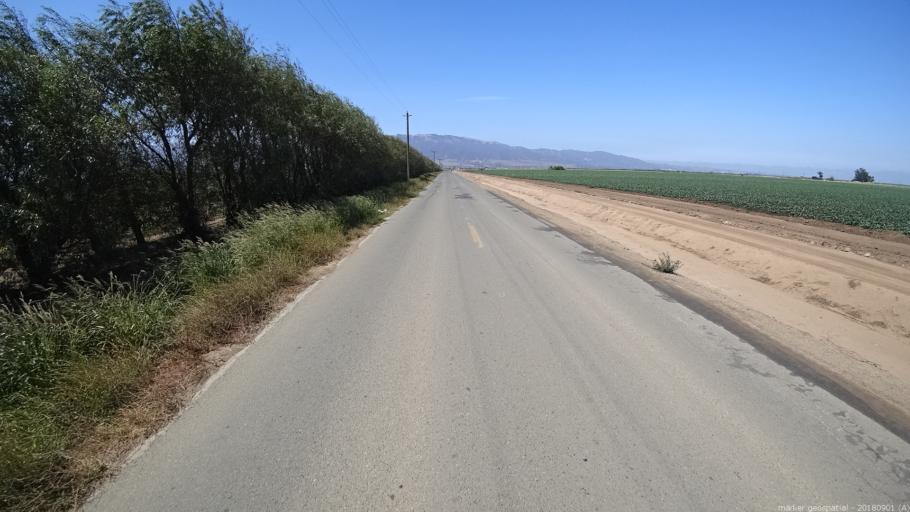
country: US
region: California
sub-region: Monterey County
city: Chualar
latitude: 36.5787
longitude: -121.4881
